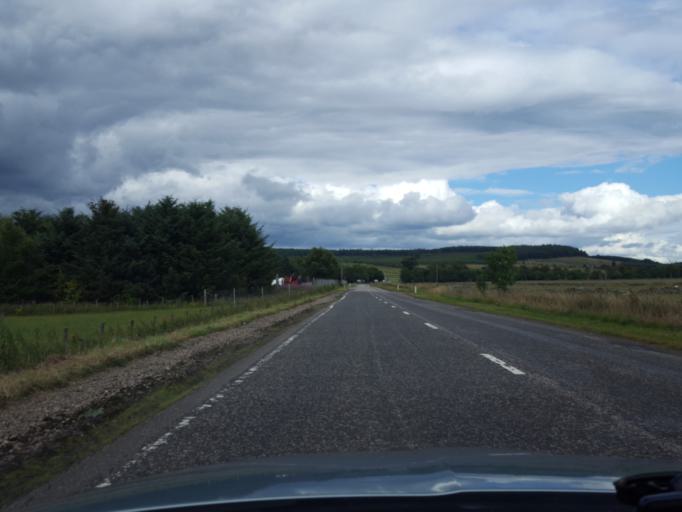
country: GB
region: Scotland
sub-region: Moray
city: Rothes
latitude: 57.4257
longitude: -3.3492
